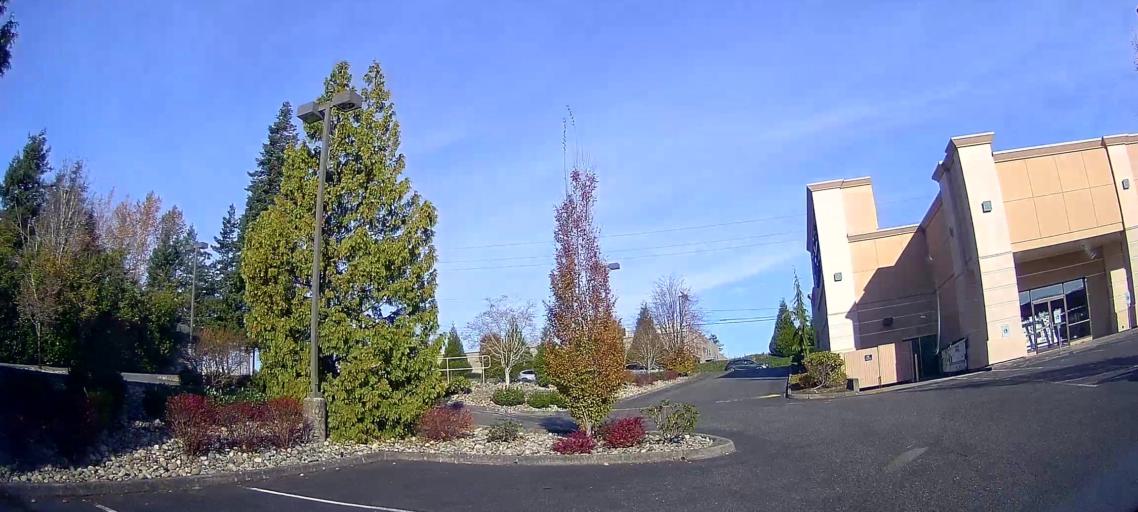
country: US
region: Washington
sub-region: Whatcom County
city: Bellingham
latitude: 48.7889
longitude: -122.4872
